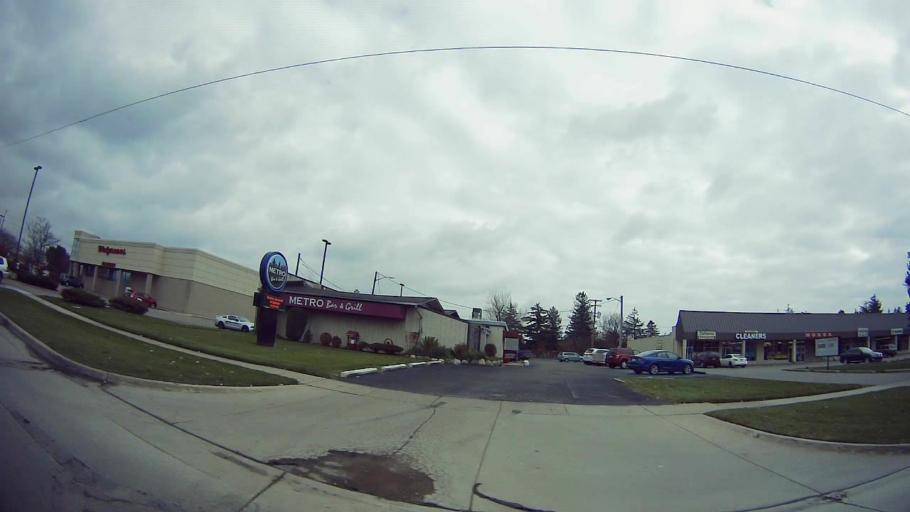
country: US
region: Michigan
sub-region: Oakland County
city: Madison Heights
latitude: 42.5203
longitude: -83.0678
